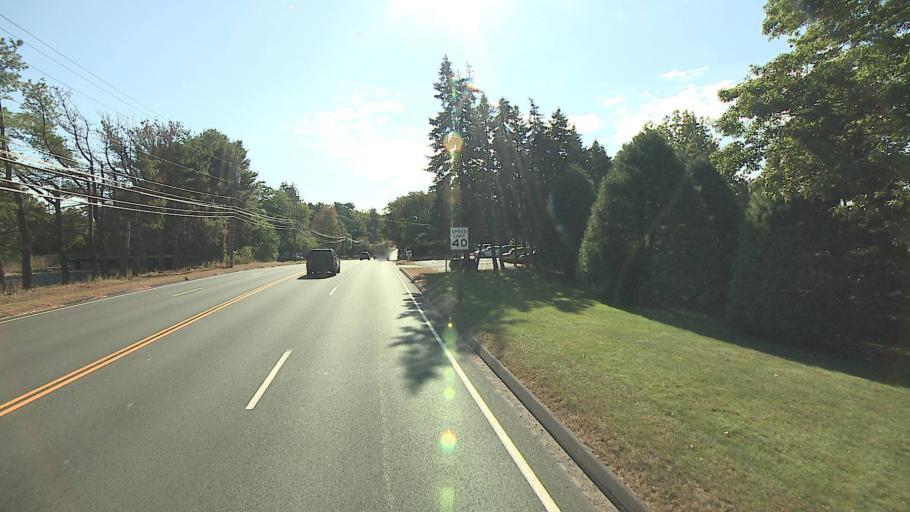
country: US
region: Connecticut
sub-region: Hartford County
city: Bristol
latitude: 41.6533
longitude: -72.9100
